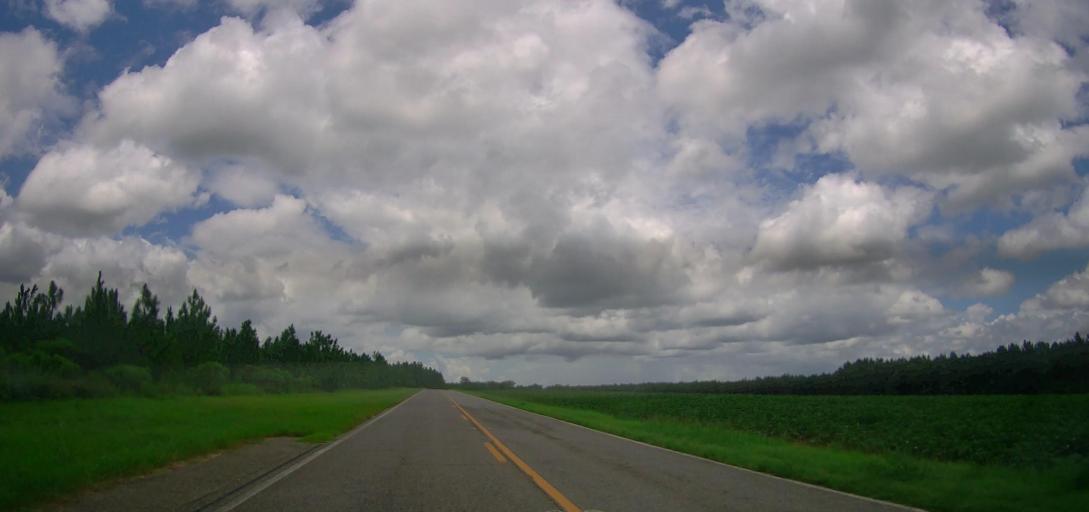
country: US
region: Georgia
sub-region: Wilcox County
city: Rochelle
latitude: 31.8725
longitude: -83.5584
